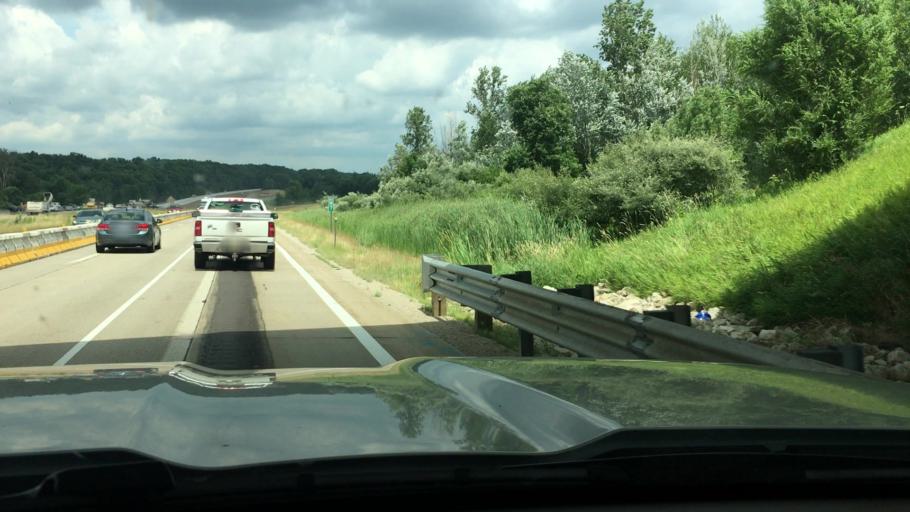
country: US
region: Michigan
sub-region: Kent County
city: Rockford
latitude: 43.1171
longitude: -85.6065
